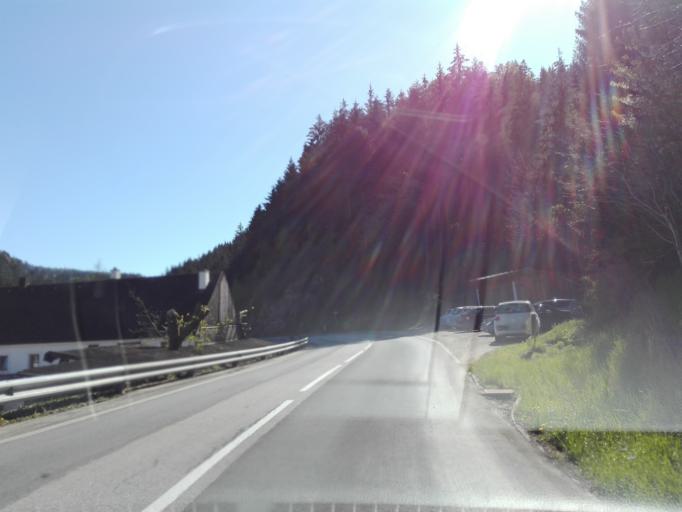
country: AT
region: Upper Austria
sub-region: Politischer Bezirk Perg
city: Bad Kreuzen
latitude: 48.3424
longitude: 14.7140
